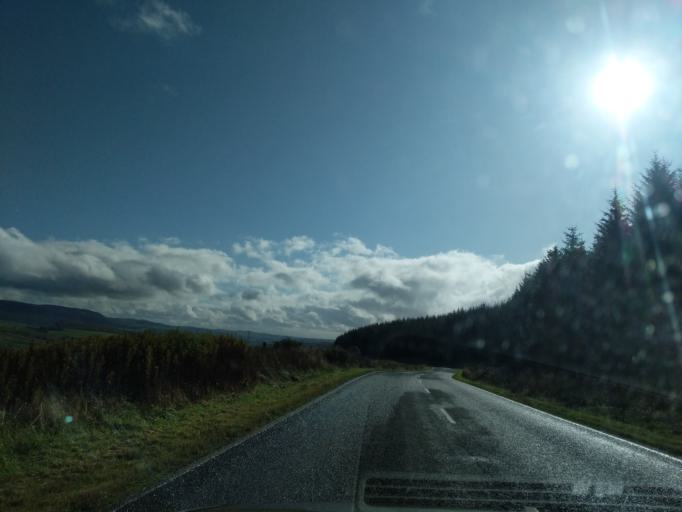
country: GB
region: Scotland
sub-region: Dumfries and Galloway
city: Moffat
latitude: 55.3735
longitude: -3.4768
